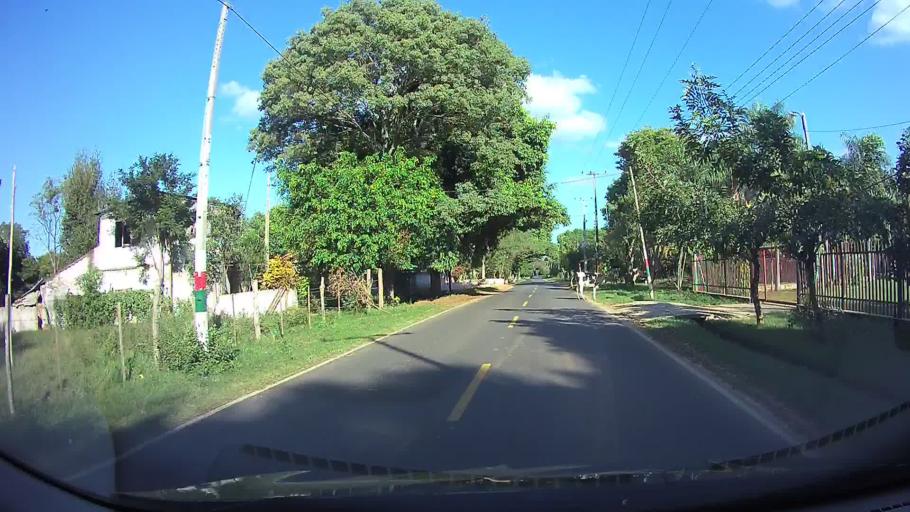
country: PY
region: Central
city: Aregua
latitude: -25.2872
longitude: -57.3954
